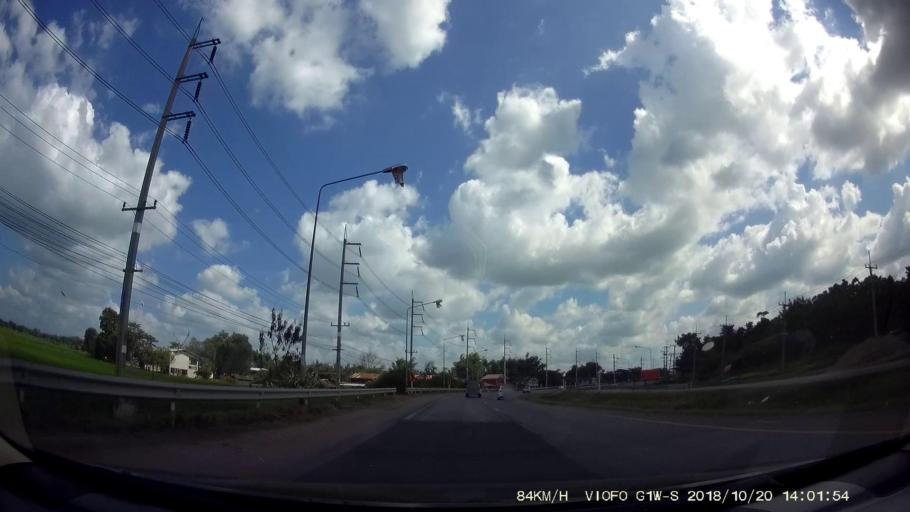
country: TH
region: Khon Kaen
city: Chum Phae
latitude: 16.4976
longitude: 102.1241
